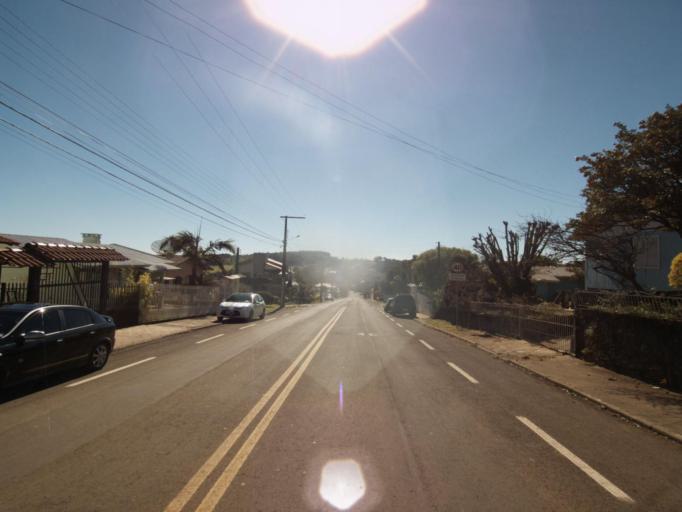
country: AR
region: Misiones
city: Bernardo de Irigoyen
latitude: -26.7196
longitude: -53.5232
